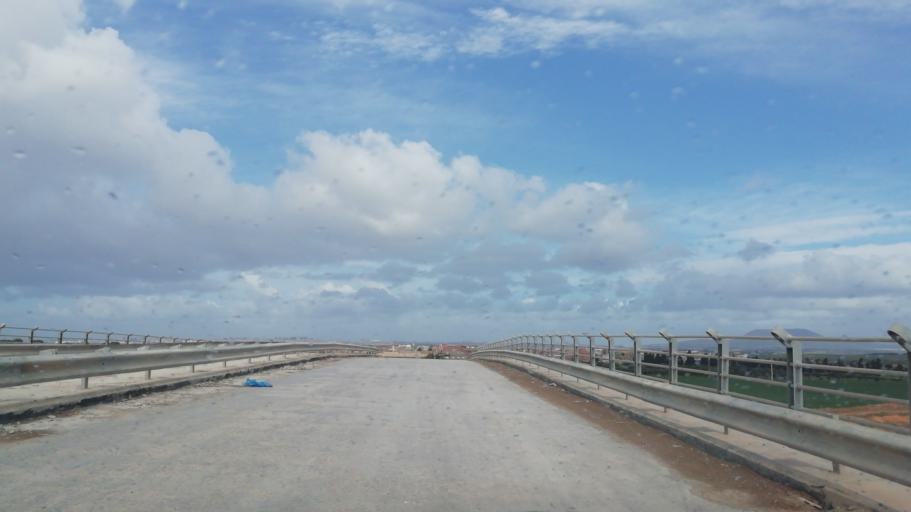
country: DZ
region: Oran
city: Sidi ech Chahmi
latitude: 35.6479
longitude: -0.5176
